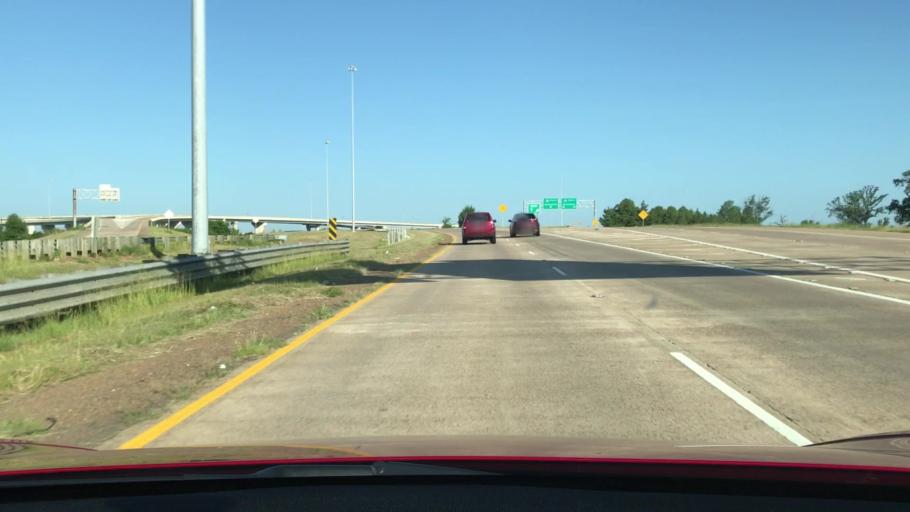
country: US
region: Louisiana
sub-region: Bossier Parish
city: Bossier City
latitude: 32.4180
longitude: -93.7429
